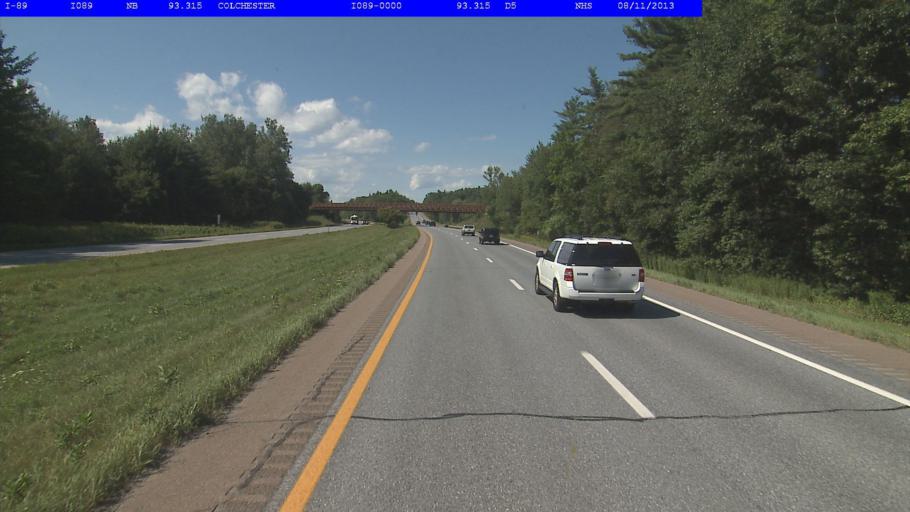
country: US
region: Vermont
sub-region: Chittenden County
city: Winooski
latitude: 44.5286
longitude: -73.1941
